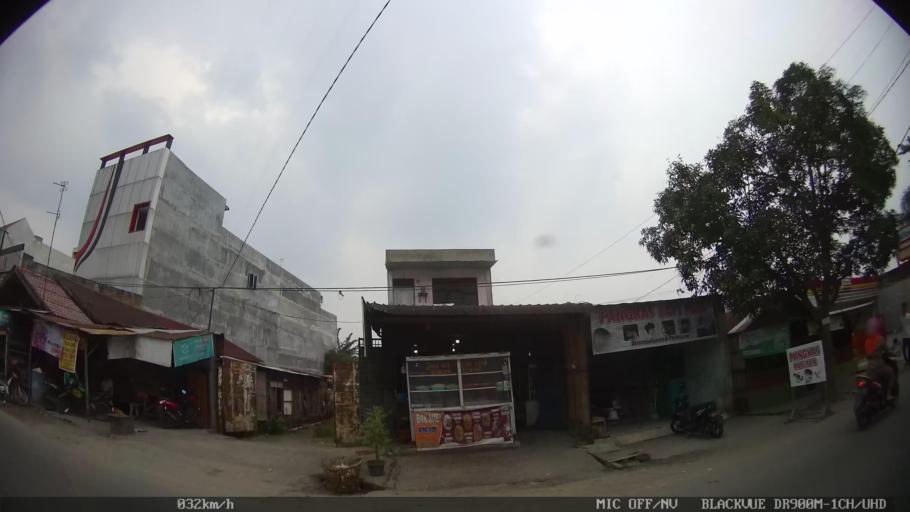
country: ID
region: North Sumatra
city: Deli Tua
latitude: 3.5526
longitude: 98.7156
